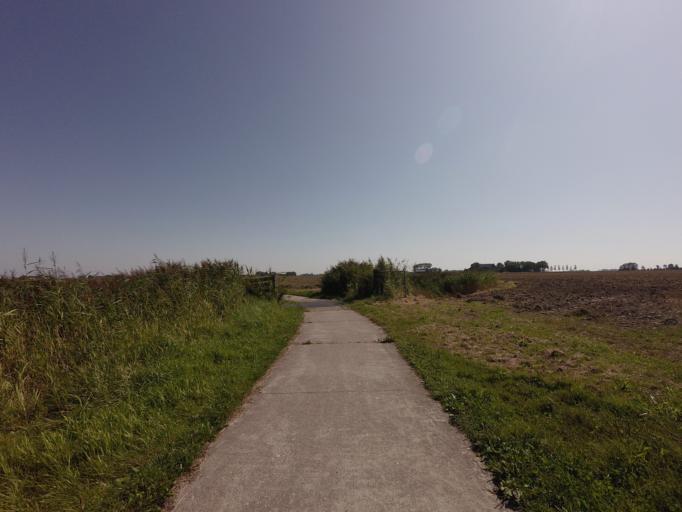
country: NL
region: Friesland
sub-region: Gemeente Dongeradeel
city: Anjum
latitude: 53.3922
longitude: 6.0677
